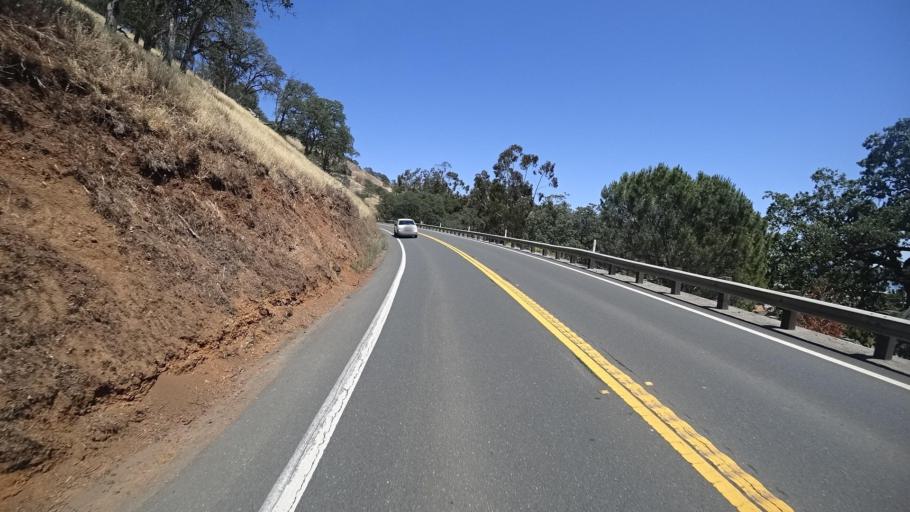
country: US
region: California
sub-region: Lake County
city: Soda Bay
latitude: 39.0381
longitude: -122.7672
